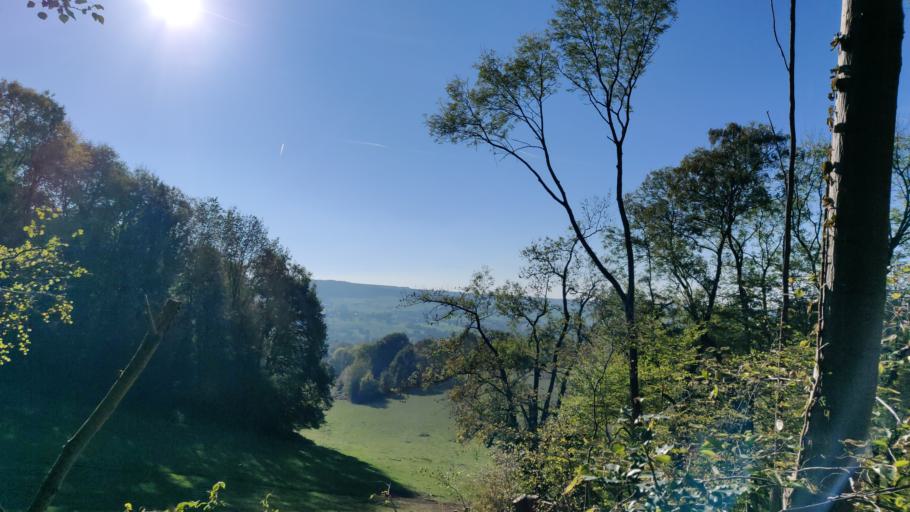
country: BE
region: Wallonia
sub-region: Province de Liege
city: Plombieres
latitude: 50.7630
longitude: 5.9550
